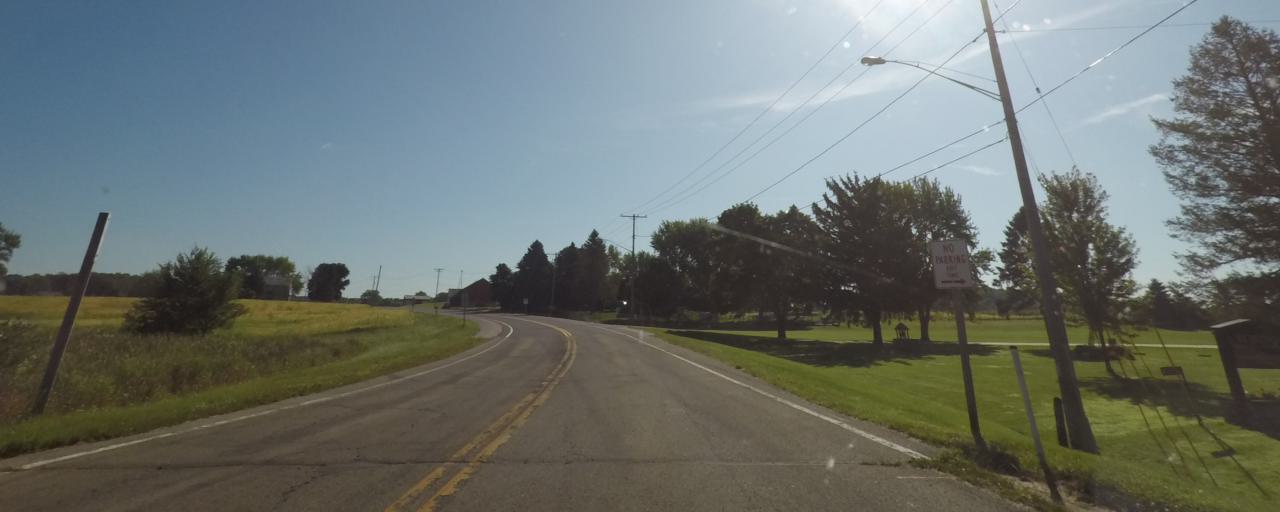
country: US
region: Wisconsin
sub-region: Jefferson County
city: Johnson Creek
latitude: 43.0119
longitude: -88.6972
